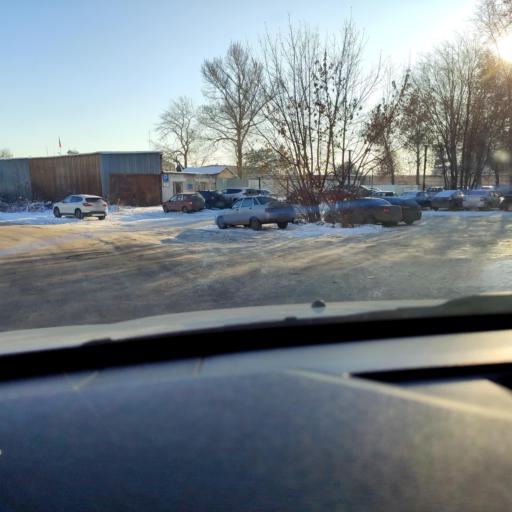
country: RU
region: Samara
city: Samara
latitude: 53.1828
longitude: 50.2168
